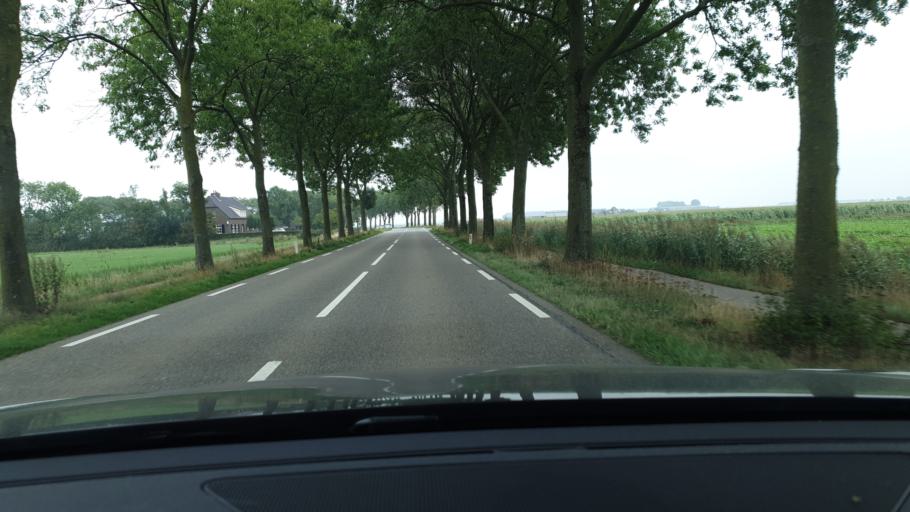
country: NL
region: North Brabant
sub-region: Gemeente 's-Hertogenbosch
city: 's-Hertogenbosch
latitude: 51.7450
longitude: 5.3583
